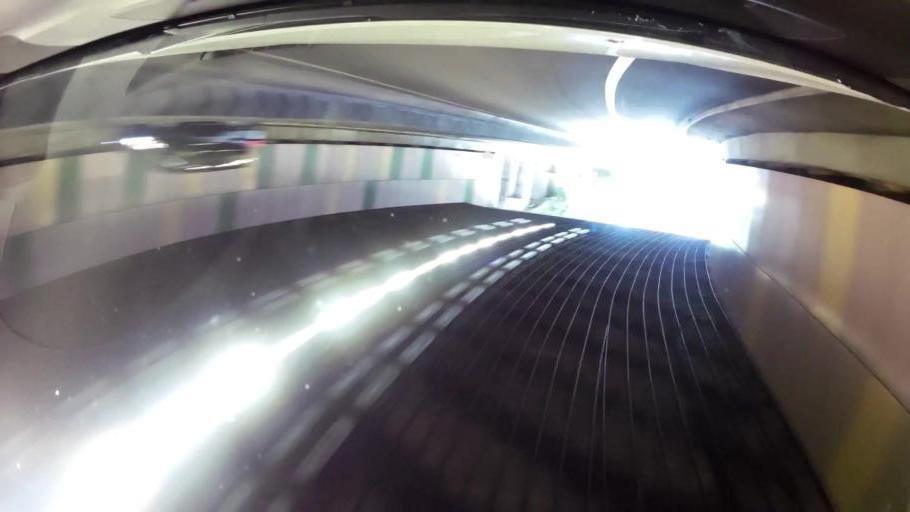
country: HK
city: Hong Kong
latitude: 22.2779
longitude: 114.1318
